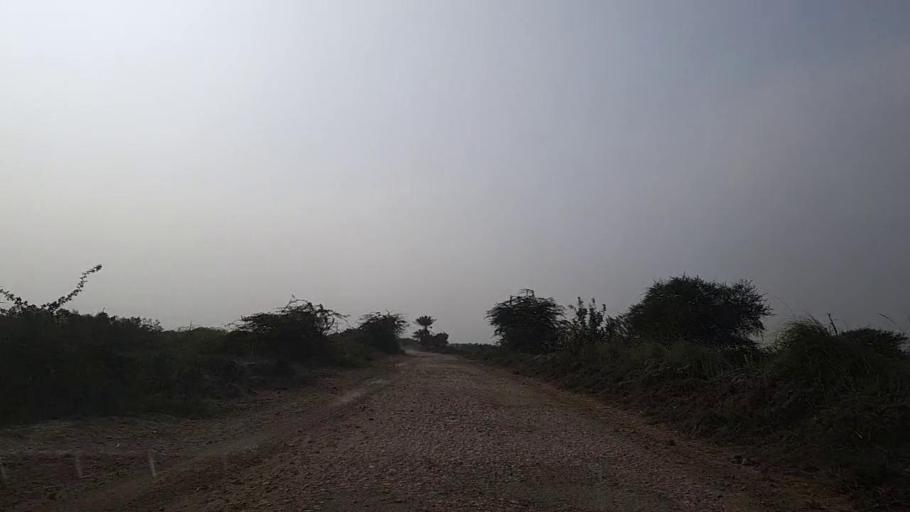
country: PK
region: Sindh
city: Gharo
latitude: 24.6496
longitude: 67.6207
